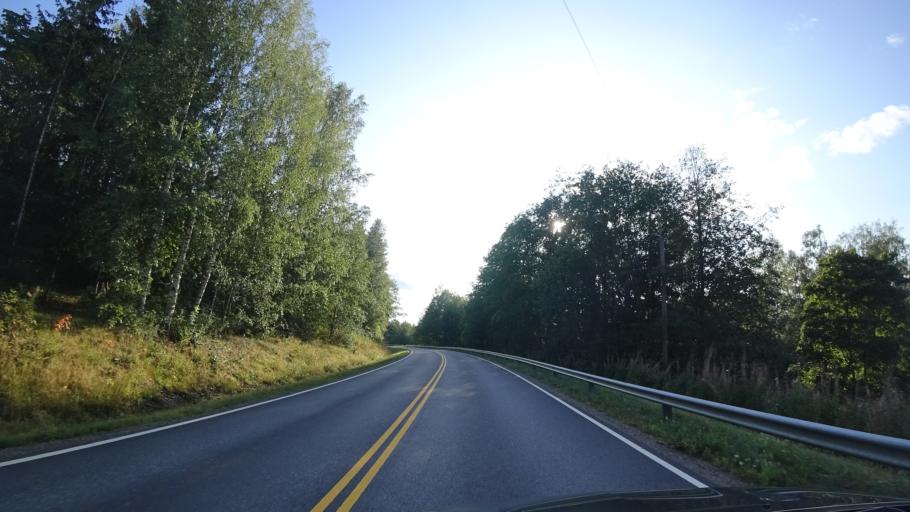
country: FI
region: Paijanne Tavastia
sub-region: Lahti
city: Hollola
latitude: 61.1437
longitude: 25.3339
